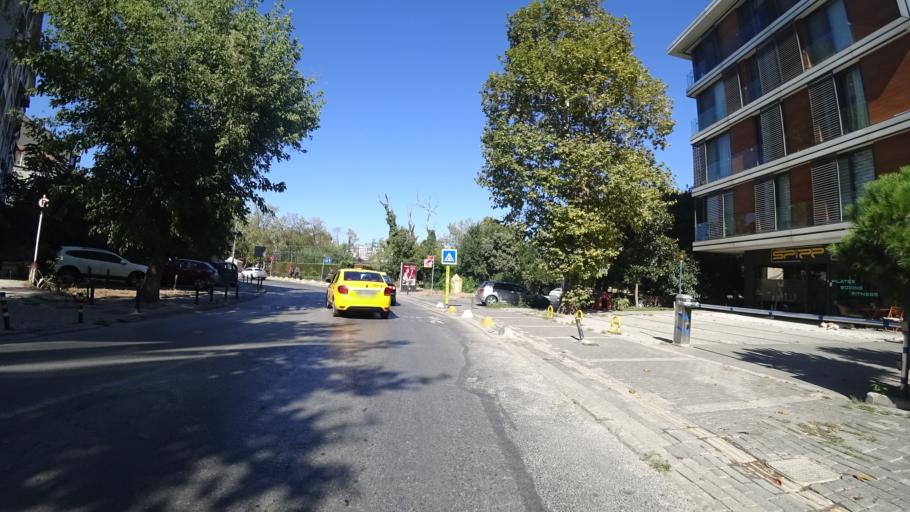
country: TR
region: Istanbul
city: UEskuedar
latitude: 40.9830
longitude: 29.0327
